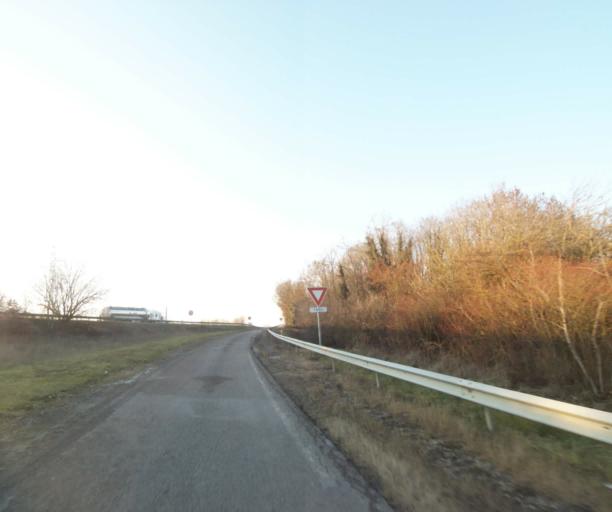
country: FR
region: Champagne-Ardenne
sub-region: Departement de la Haute-Marne
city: Chevillon
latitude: 48.5417
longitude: 5.0854
